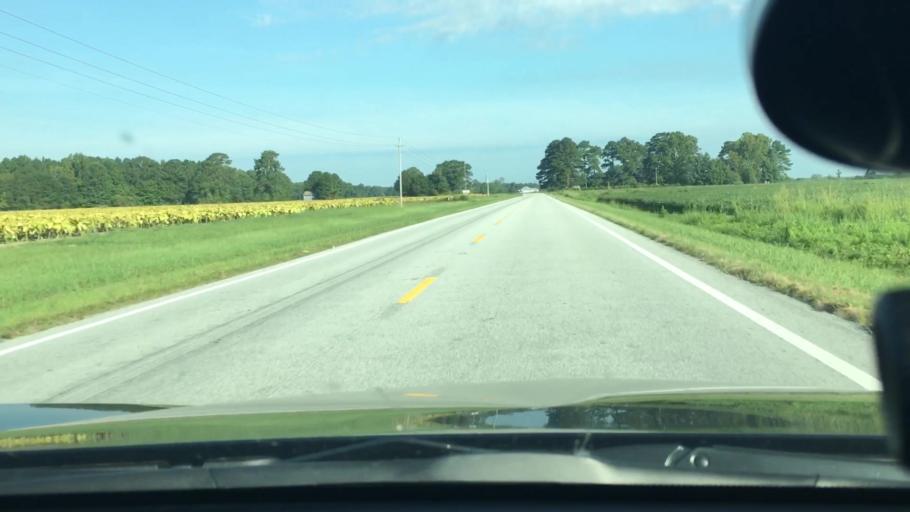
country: US
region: North Carolina
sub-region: Pitt County
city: Summerfield
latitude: 35.6654
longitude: -77.4769
